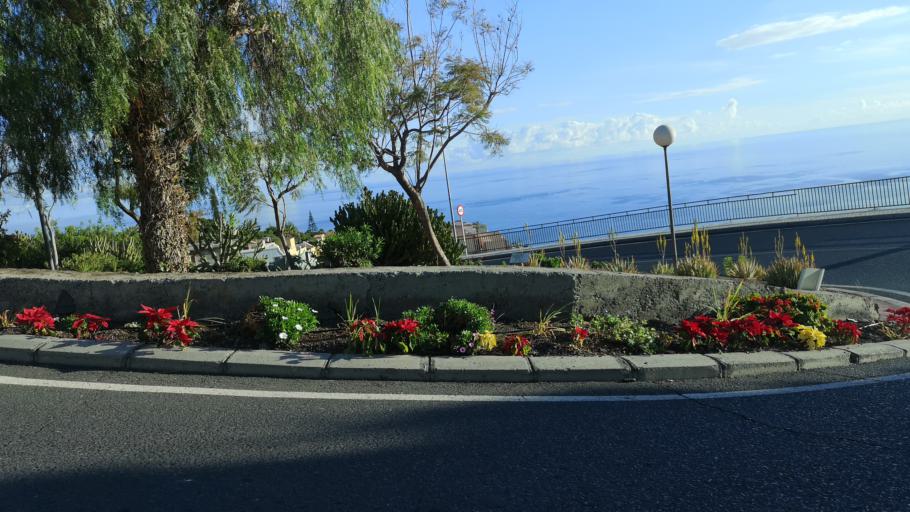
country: ES
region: Canary Islands
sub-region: Provincia de Santa Cruz de Tenerife
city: Alajero
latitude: 28.0350
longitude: -17.1921
